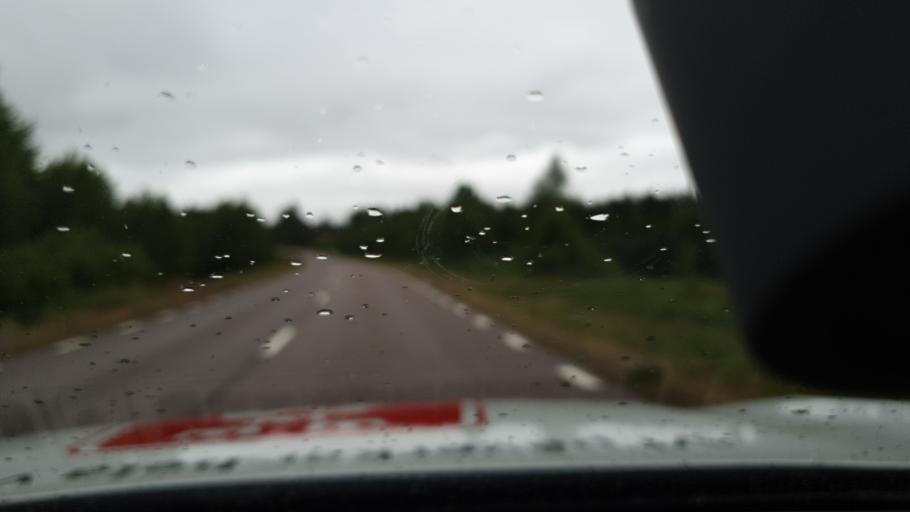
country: FI
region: Lapland
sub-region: Torniolaakso
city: Pello
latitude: 66.9666
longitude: 23.8193
